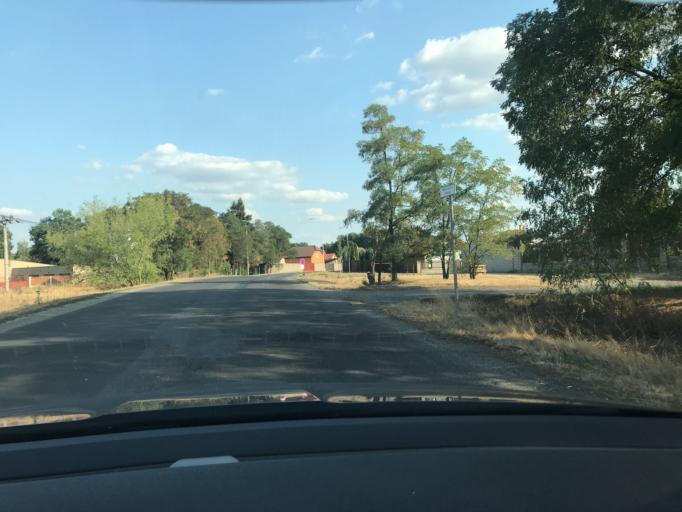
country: CZ
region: Ustecky
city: Postoloprty
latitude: 50.3646
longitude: 13.6900
